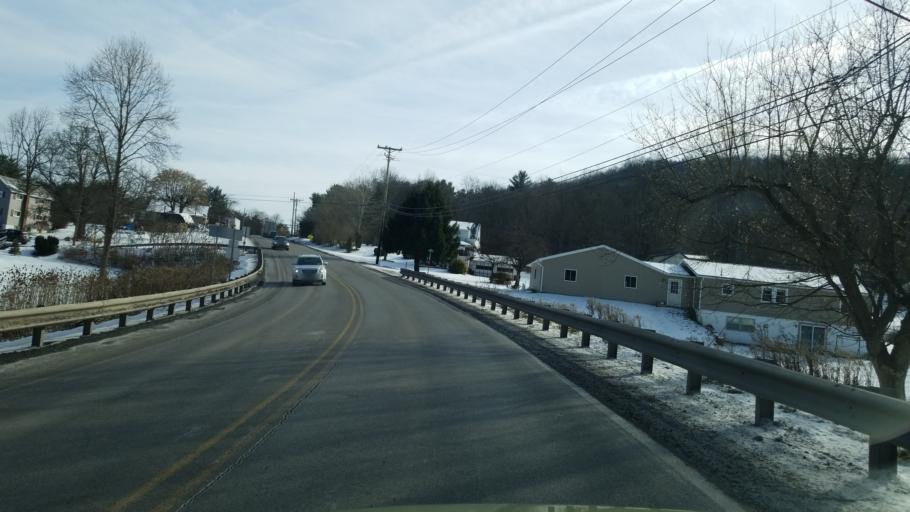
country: US
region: Pennsylvania
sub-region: Clearfield County
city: Treasure Lake
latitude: 41.2063
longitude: -78.5724
